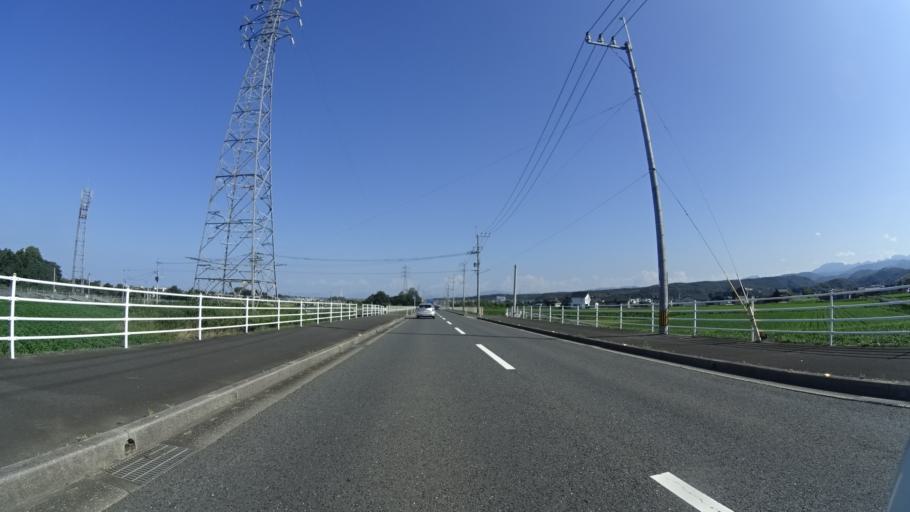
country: JP
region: Fukuoka
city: Tsuiki
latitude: 33.6579
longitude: 131.0408
